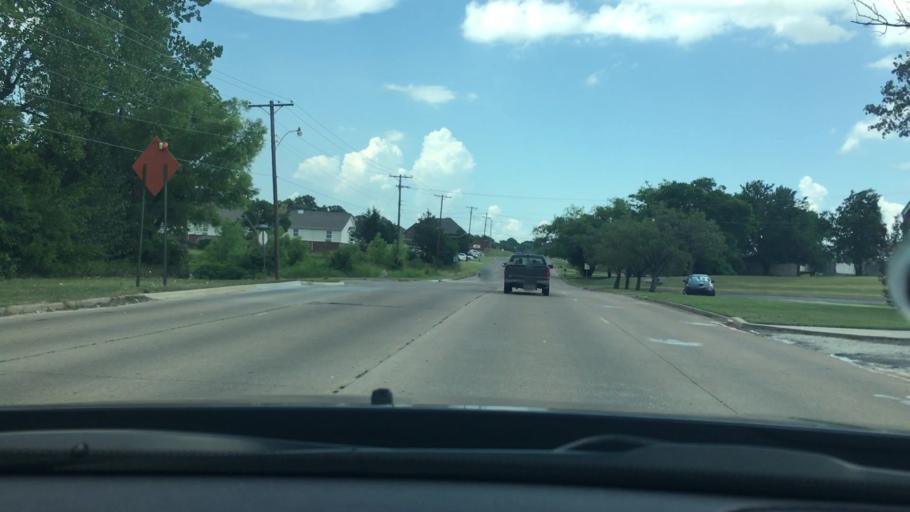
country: US
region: Oklahoma
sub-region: Pontotoc County
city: Ada
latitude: 34.7648
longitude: -96.6611
